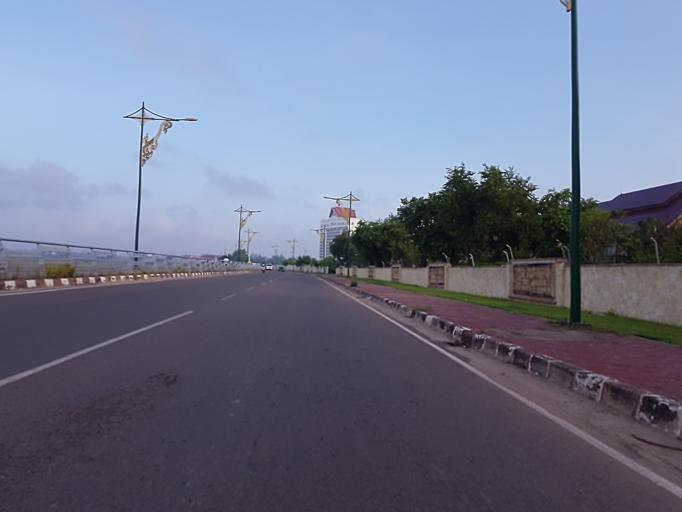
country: LA
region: Vientiane
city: Vientiane
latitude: 17.9500
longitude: 102.6155
